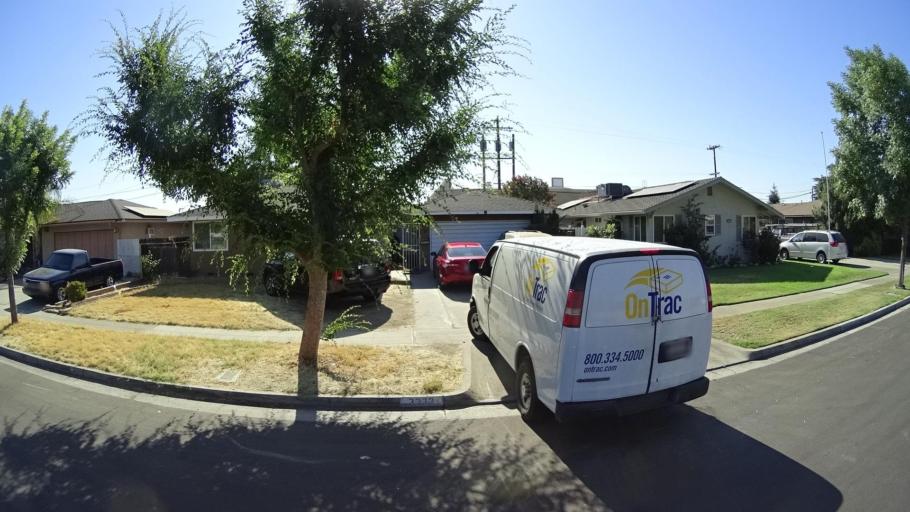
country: US
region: California
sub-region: Fresno County
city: Fresno
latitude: 36.7804
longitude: -119.7567
